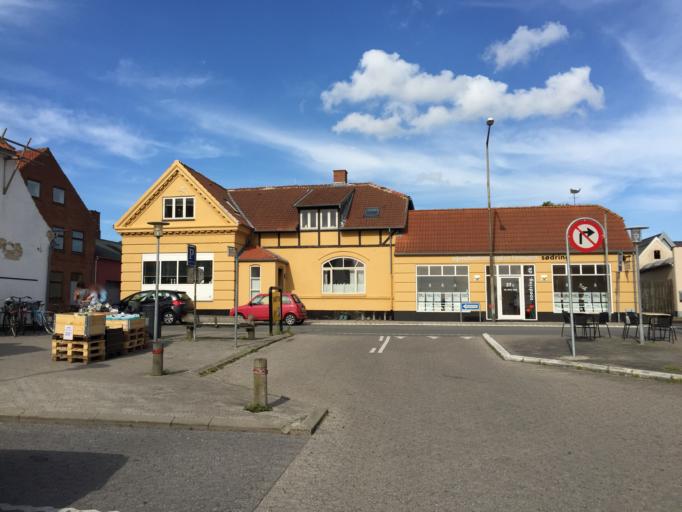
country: DK
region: Capital Region
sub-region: Halsnaes Kommune
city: Hundested
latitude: 55.9619
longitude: 11.8511
